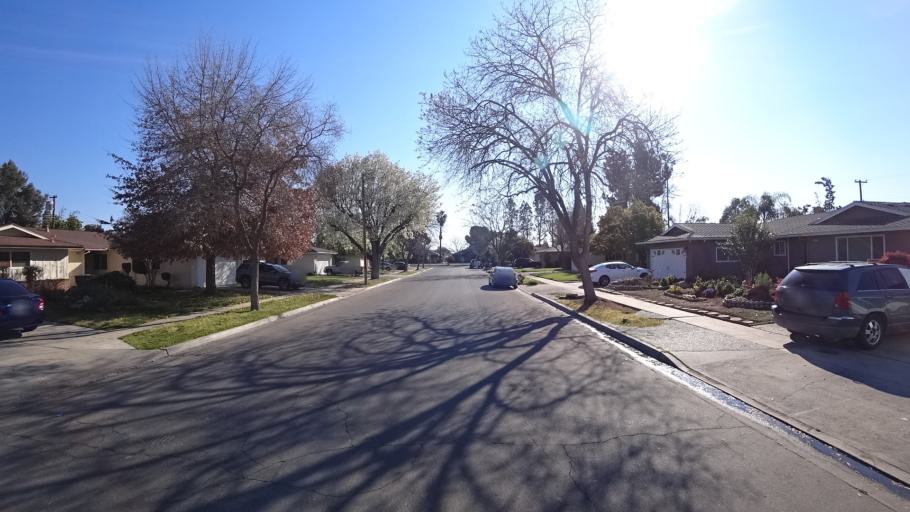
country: US
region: California
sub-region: Fresno County
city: Clovis
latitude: 36.8272
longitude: -119.7735
